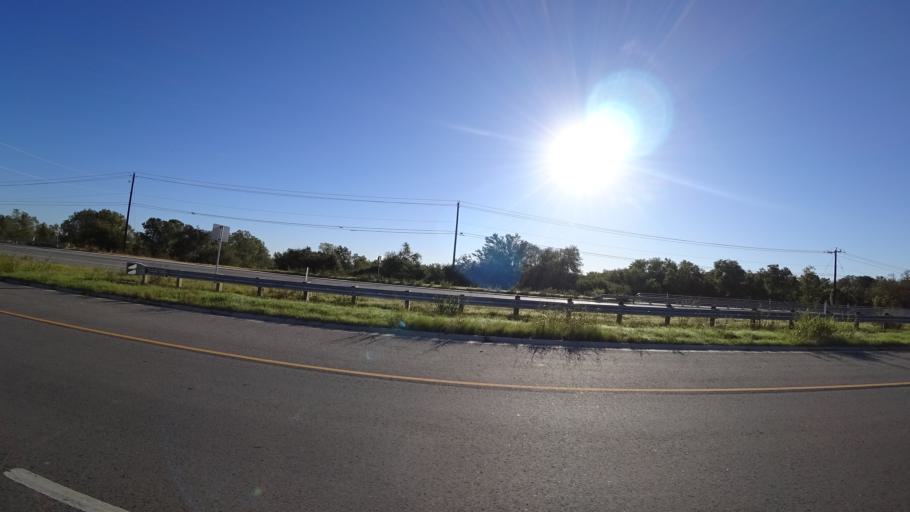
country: US
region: Texas
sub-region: Travis County
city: Hornsby Bend
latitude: 30.2097
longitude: -97.6381
